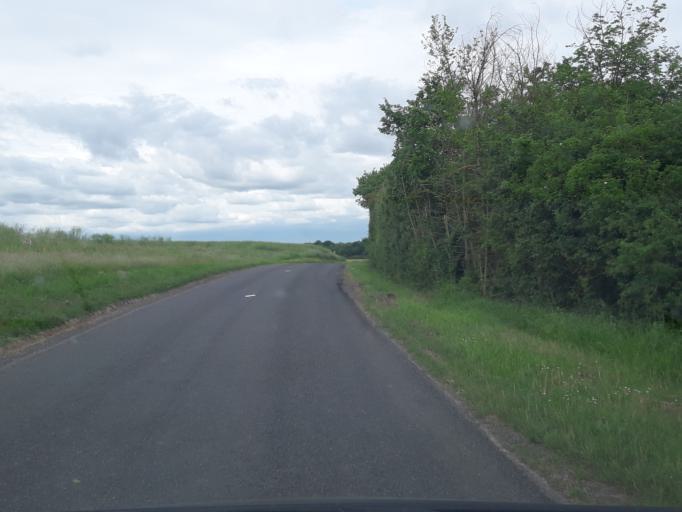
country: FR
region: Ile-de-France
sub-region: Departement de l'Essonne
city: Boissy-le-Cutte
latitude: 48.4151
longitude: 2.2801
